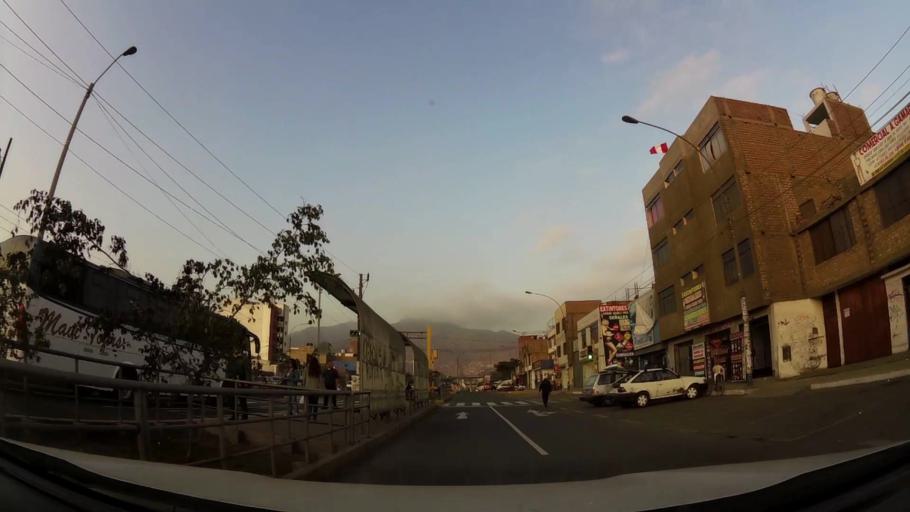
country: PE
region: Lima
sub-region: Lima
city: Independencia
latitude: -12.0054
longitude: -77.0666
